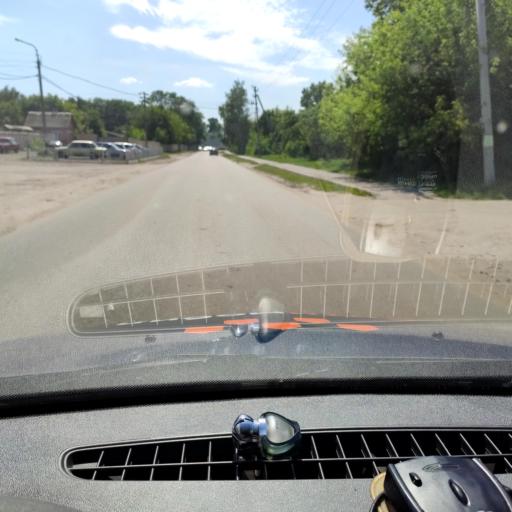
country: RU
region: Voronezj
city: Ramon'
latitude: 51.8267
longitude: 39.2653
